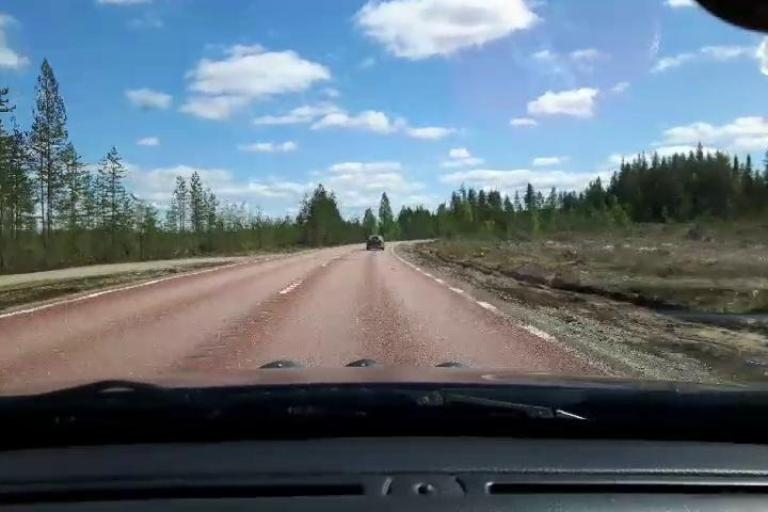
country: SE
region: Gaevleborg
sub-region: Ljusdals Kommun
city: Farila
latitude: 61.8998
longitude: 15.6470
